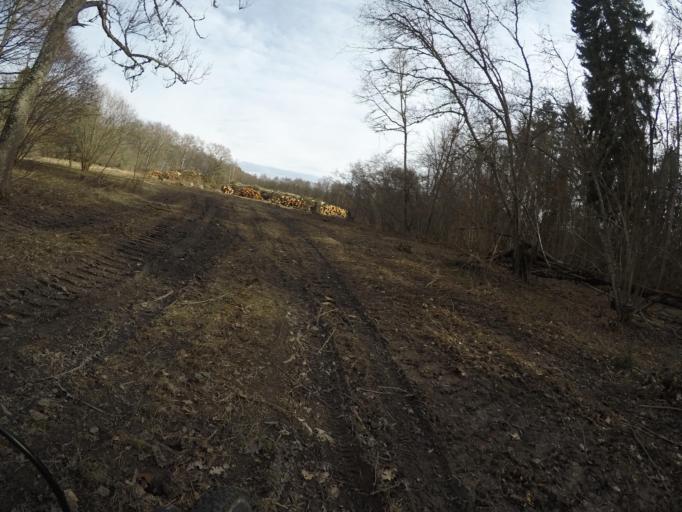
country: SE
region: Soedermanland
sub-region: Eskilstuna Kommun
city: Hallbybrunn
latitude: 59.4522
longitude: 16.3984
